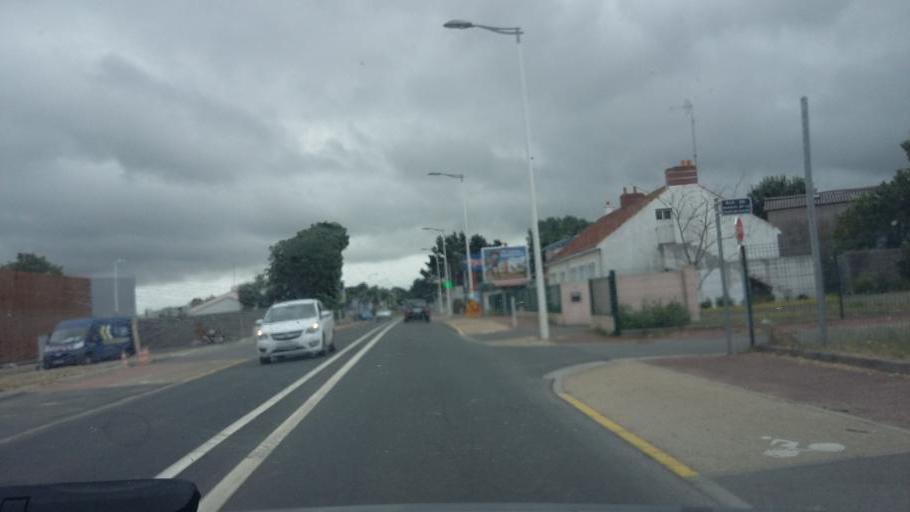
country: FR
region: Pays de la Loire
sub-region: Departement de la Vendee
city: Challans
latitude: 46.8535
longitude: -1.8942
